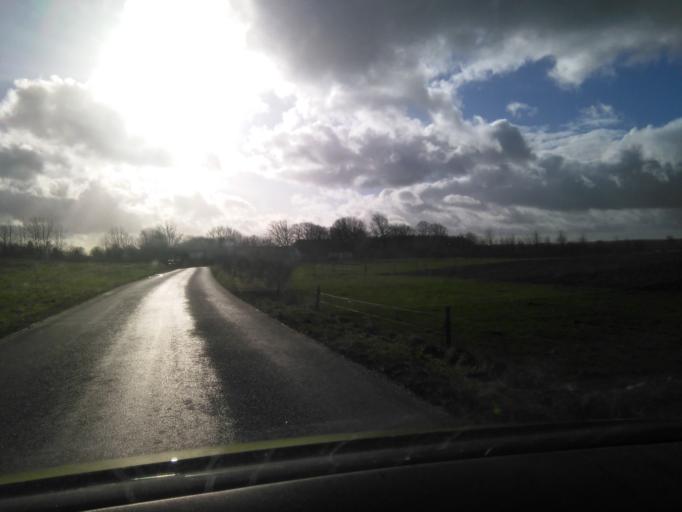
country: DK
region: Central Jutland
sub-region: Arhus Kommune
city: Beder
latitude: 56.0629
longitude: 10.2434
